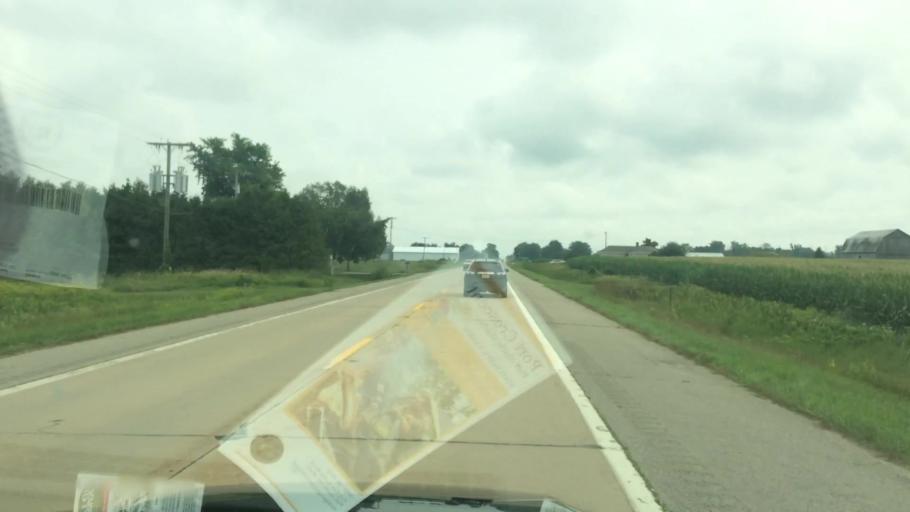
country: US
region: Michigan
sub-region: Huron County
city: Bad Axe
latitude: 44.0421
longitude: -82.9556
